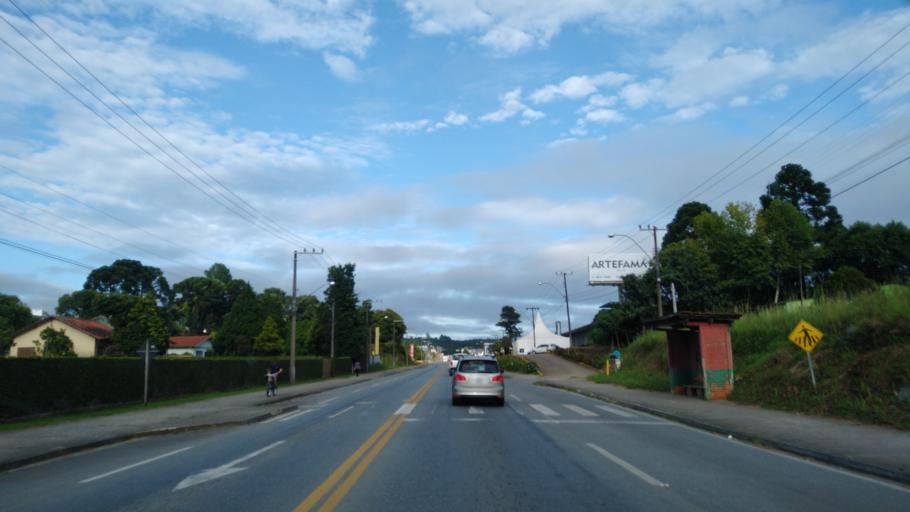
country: BR
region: Santa Catarina
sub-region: Sao Bento Do Sul
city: Sao Bento do Sul
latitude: -26.2241
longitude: -49.4051
